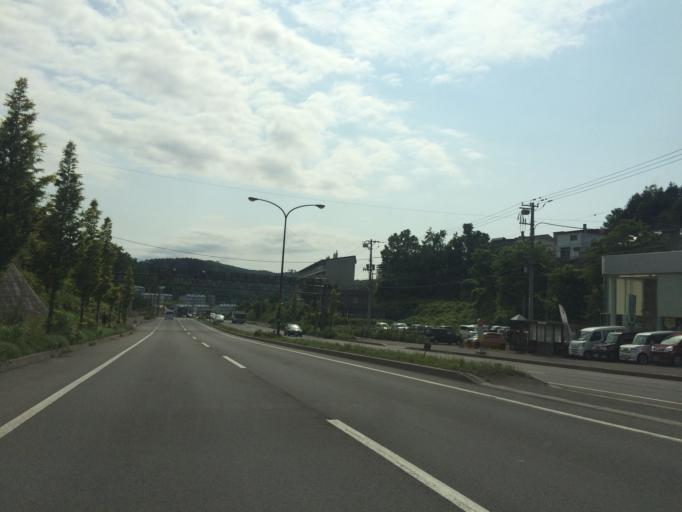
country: JP
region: Hokkaido
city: Otaru
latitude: 43.2123
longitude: 140.9366
